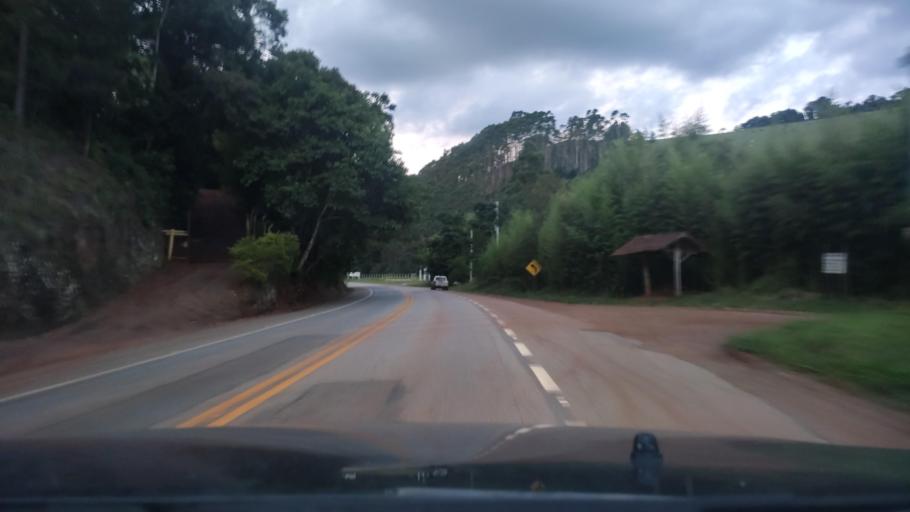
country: BR
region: Sao Paulo
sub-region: Campos Do Jordao
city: Campos do Jordao
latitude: -22.7966
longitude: -45.7479
